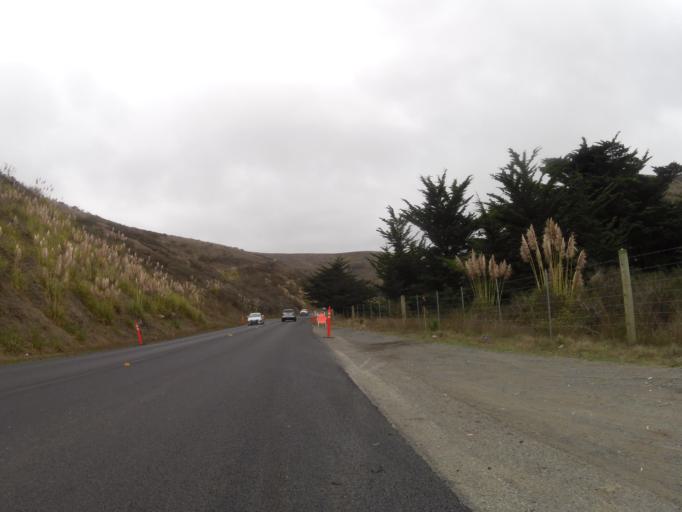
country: US
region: California
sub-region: Sonoma County
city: Bodega Bay
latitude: 38.3237
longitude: -123.0117
